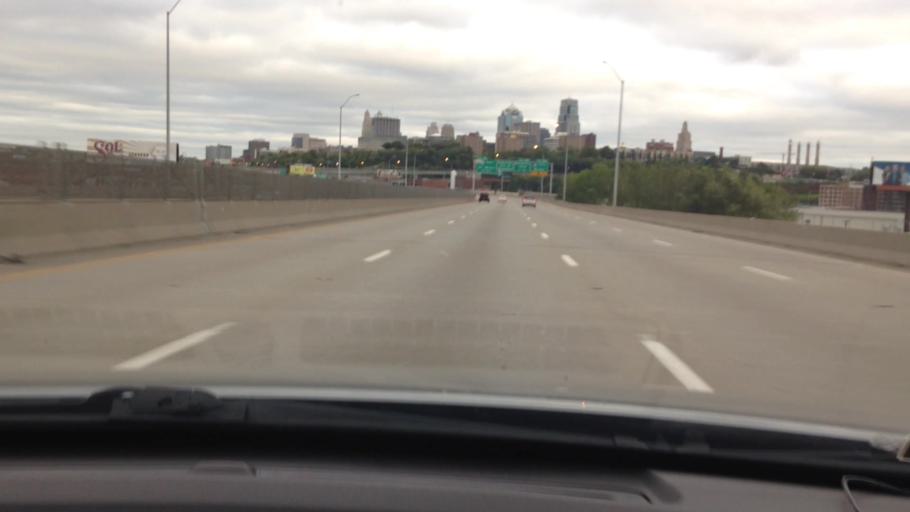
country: US
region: Kansas
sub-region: Wyandotte County
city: Kansas City
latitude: 39.1086
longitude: -94.6078
